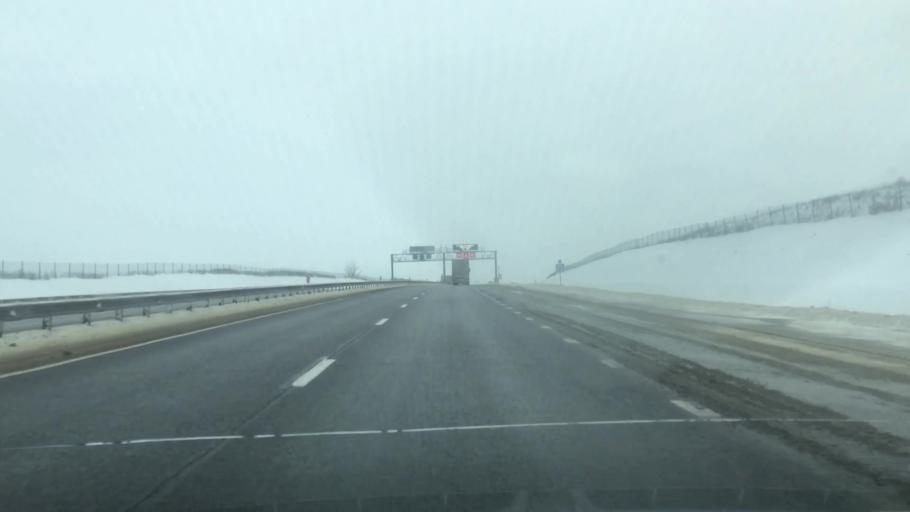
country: RU
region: Tula
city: Yefremov
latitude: 53.1566
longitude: 38.2501
